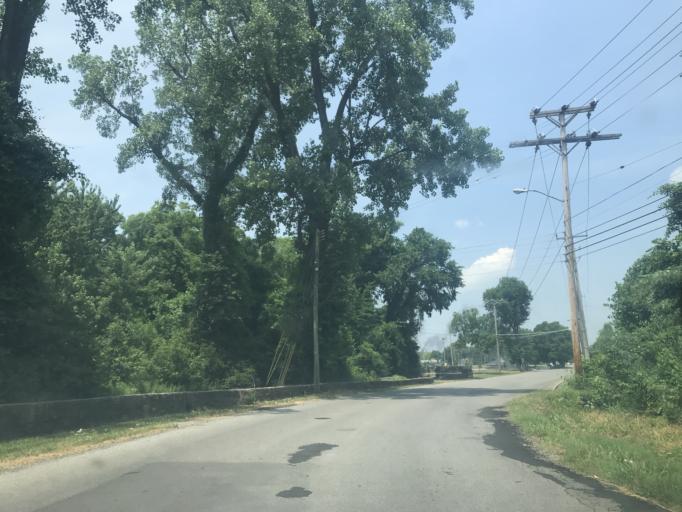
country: US
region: Tennessee
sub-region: Davidson County
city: Nashville
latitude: 36.1893
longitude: -86.8057
